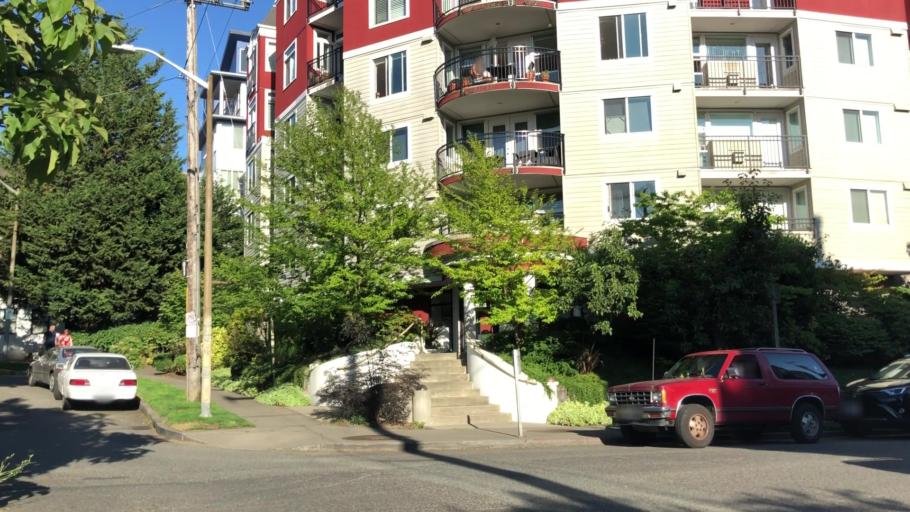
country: US
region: Washington
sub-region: King County
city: Seattle
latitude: 47.6208
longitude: -122.3241
